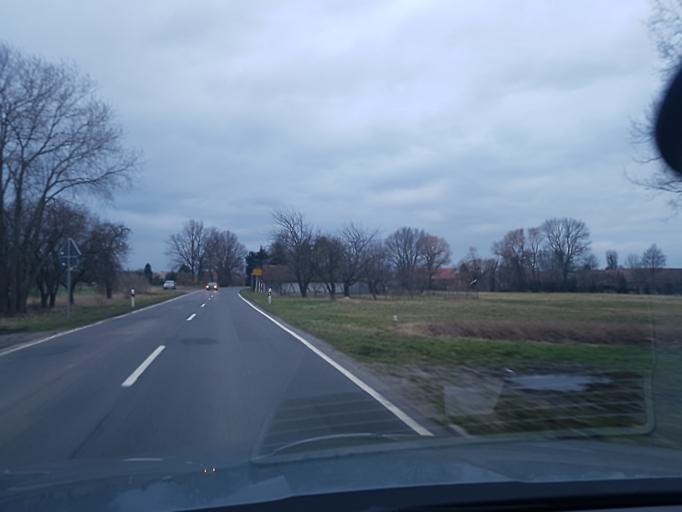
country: DE
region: Brandenburg
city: Schonewalde
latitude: 51.6622
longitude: 13.5902
